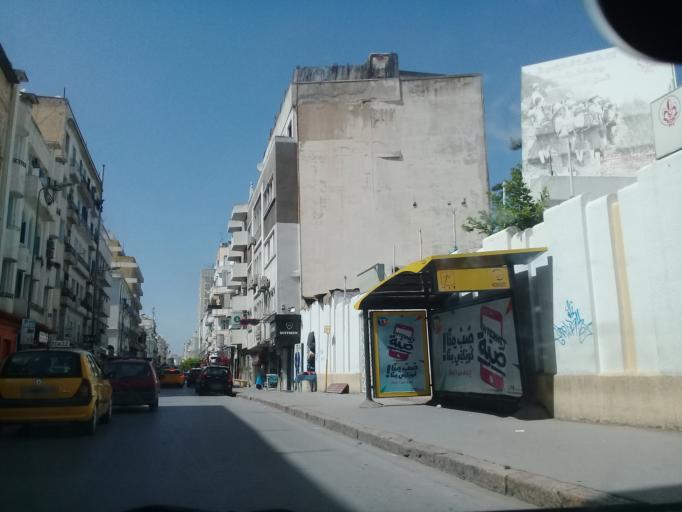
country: TN
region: Tunis
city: Tunis
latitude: 36.8104
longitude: 10.1808
